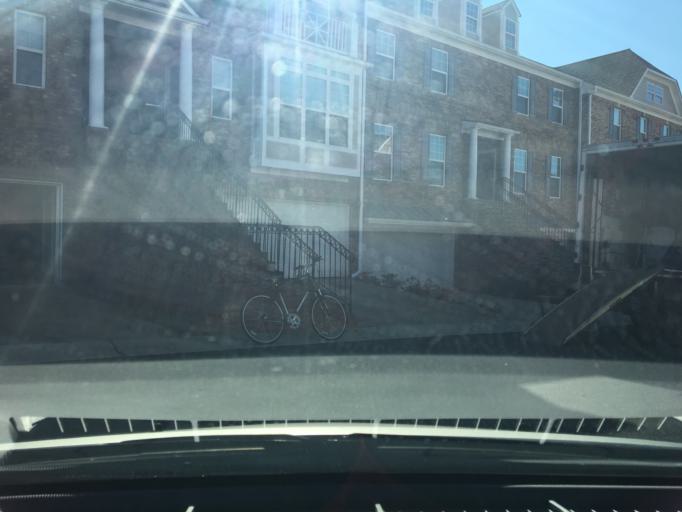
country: US
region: Georgia
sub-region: Fulton County
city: Johns Creek
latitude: 34.0461
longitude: -84.1800
